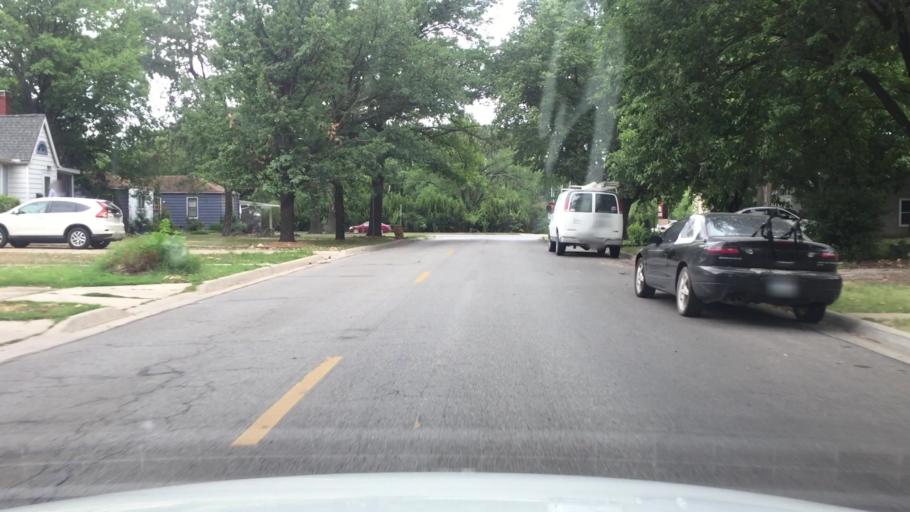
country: US
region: Kansas
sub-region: Douglas County
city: Lawrence
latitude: 38.9437
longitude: -95.2394
